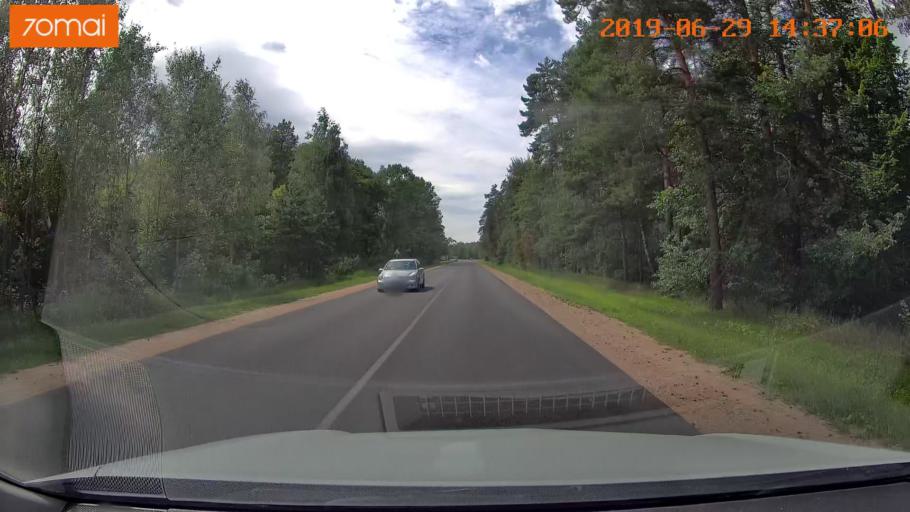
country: BY
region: Minsk
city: Starobin
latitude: 52.7504
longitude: 27.4711
